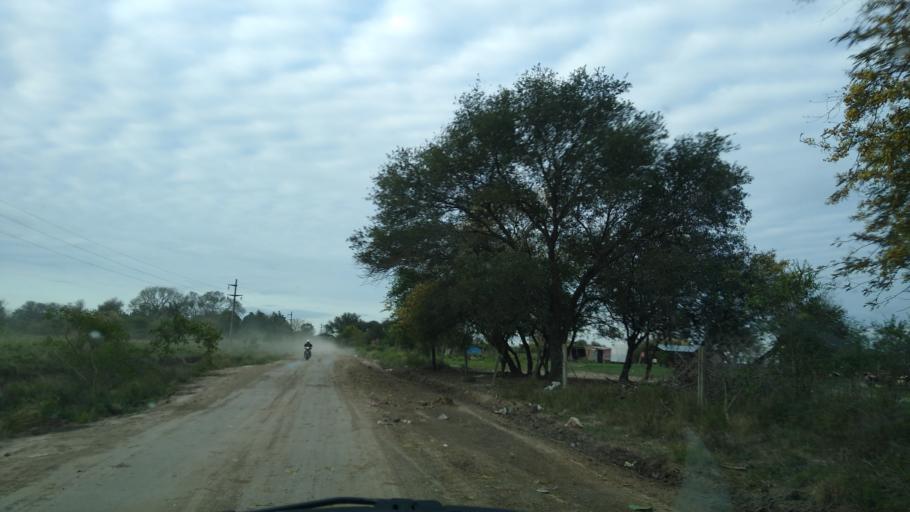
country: AR
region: Chaco
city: Fontana
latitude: -27.3839
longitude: -59.0425
